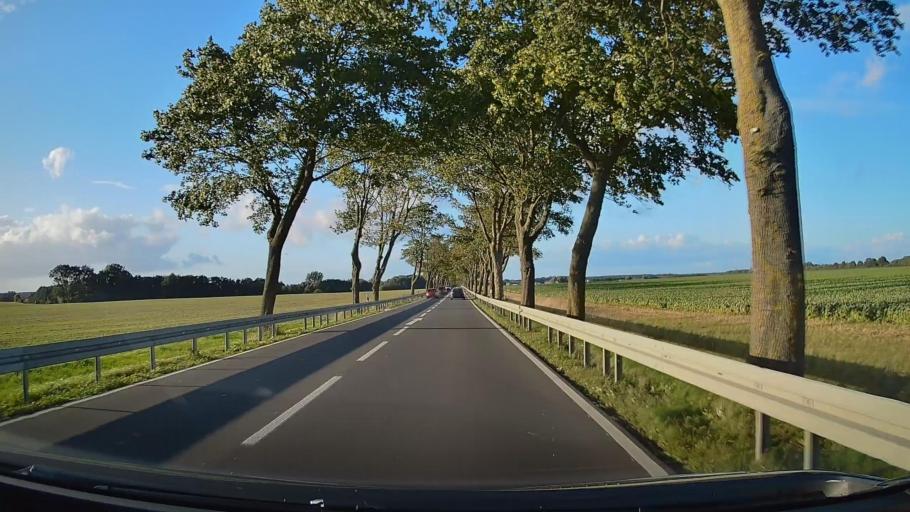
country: DE
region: Mecklenburg-Vorpommern
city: Steinhagen
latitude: 54.2143
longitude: 13.0054
